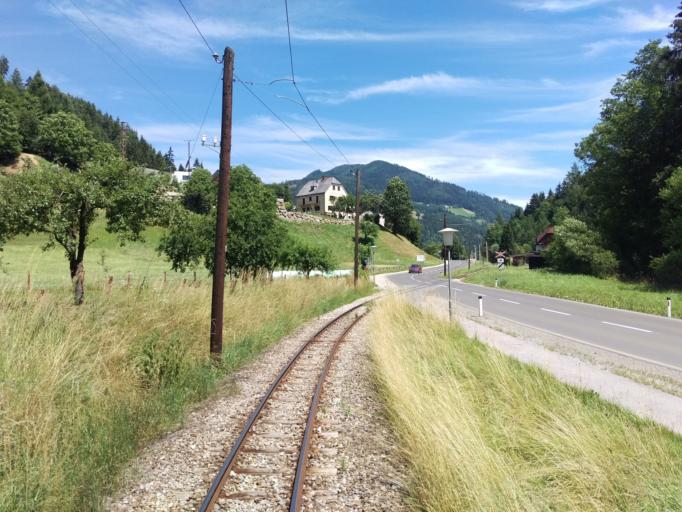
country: AT
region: Styria
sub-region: Politischer Bezirk Bruck-Muerzzuschlag
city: Allerheiligen im Muerztal
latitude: 47.3886
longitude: 15.4174
